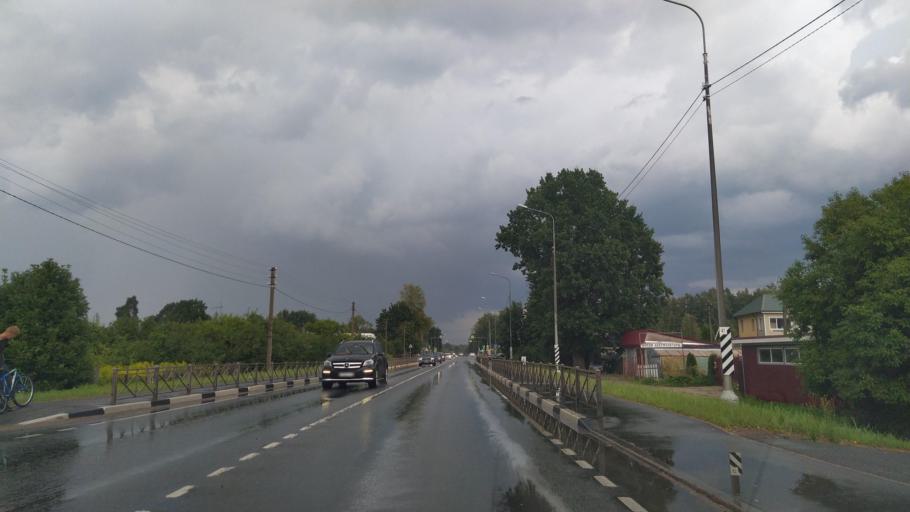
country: RU
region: Pskov
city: Pskov
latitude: 57.7463
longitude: 28.3724
